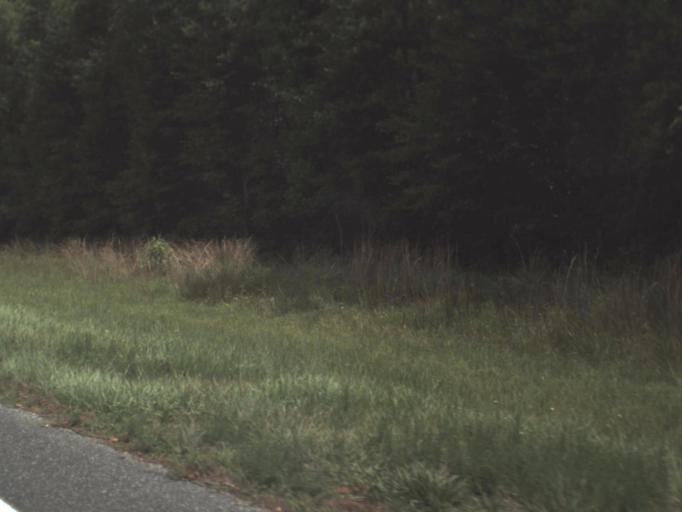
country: US
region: Florida
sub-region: Taylor County
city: Perry
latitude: 29.9711
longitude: -83.4799
